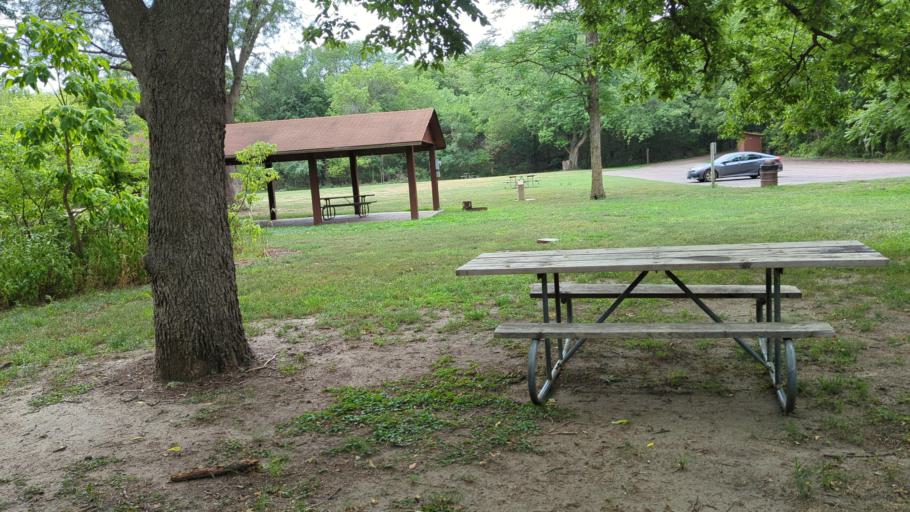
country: US
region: South Dakota
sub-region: Union County
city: Beresford
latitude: 42.9255
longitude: -96.7801
